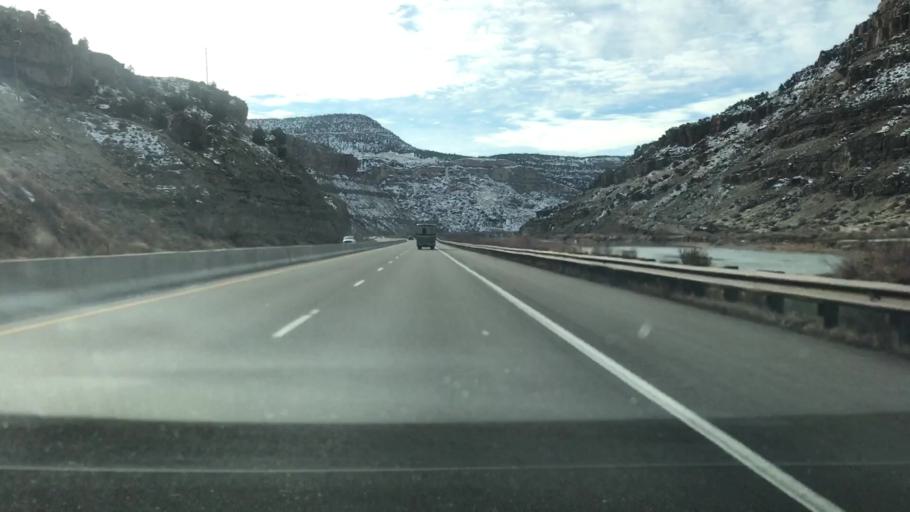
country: US
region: Colorado
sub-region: Mesa County
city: Palisade
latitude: 39.2206
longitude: -108.2562
